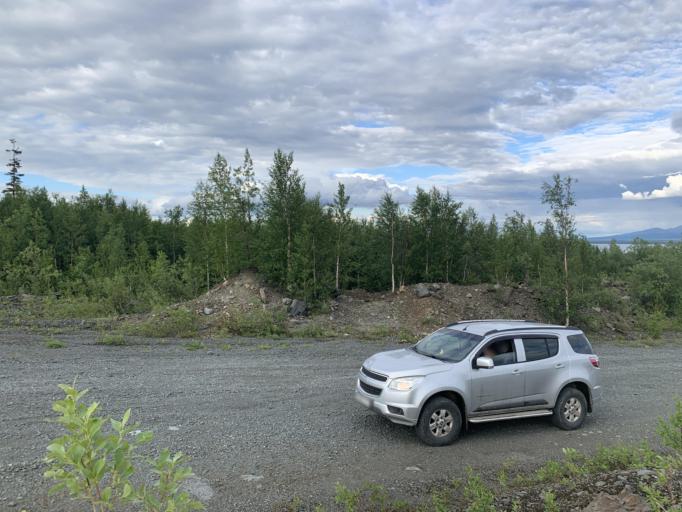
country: RU
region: Murmansk
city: Monchegorsk
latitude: 67.8910
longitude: 33.0259
